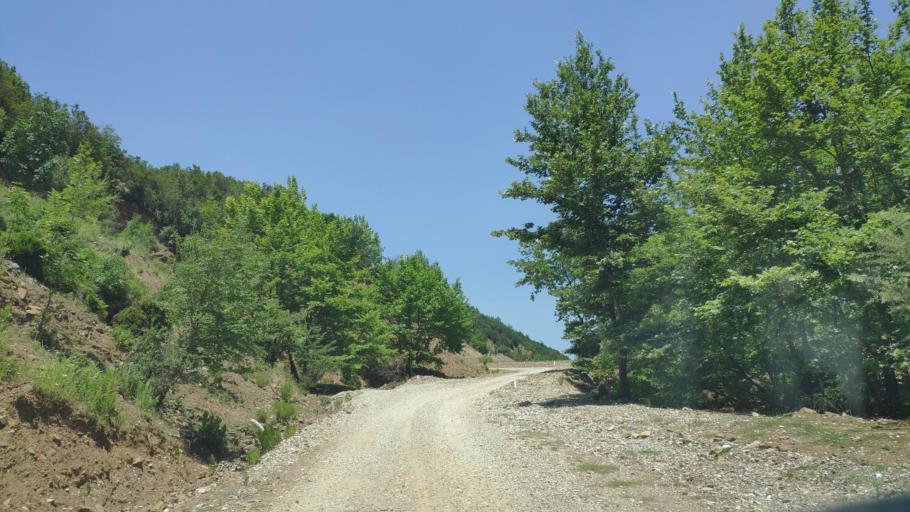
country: GR
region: Thessaly
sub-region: Nomos Kardhitsas
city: Anthiro
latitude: 39.1696
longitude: 21.3716
